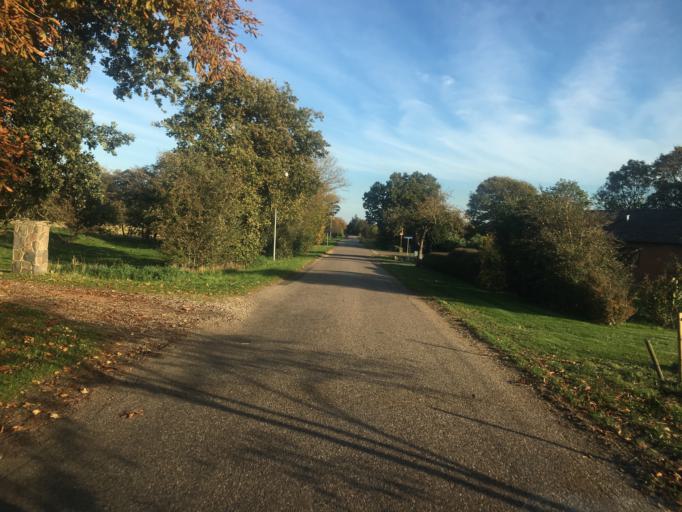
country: DK
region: South Denmark
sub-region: Tonder Kommune
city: Tonder
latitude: 54.9149
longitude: 8.9110
